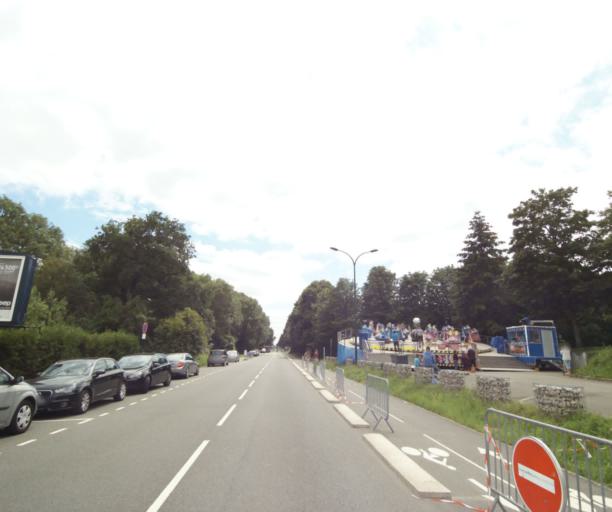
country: FR
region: Ile-de-France
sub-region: Departement des Yvelines
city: Saint-Cyr-l'Ecole
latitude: 48.7934
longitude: 2.0634
